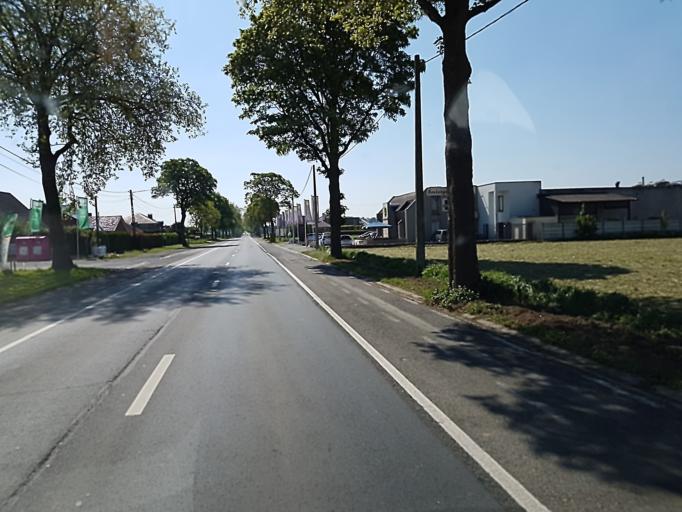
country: BE
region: Wallonia
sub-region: Province du Hainaut
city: Lens
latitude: 50.5476
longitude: 3.9039
